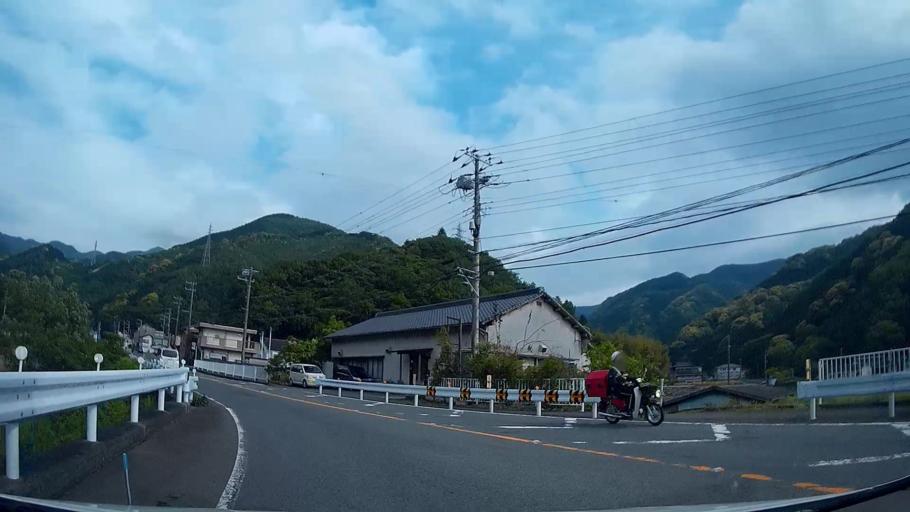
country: JP
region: Shizuoka
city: Heda
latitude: 34.9064
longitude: 138.8028
